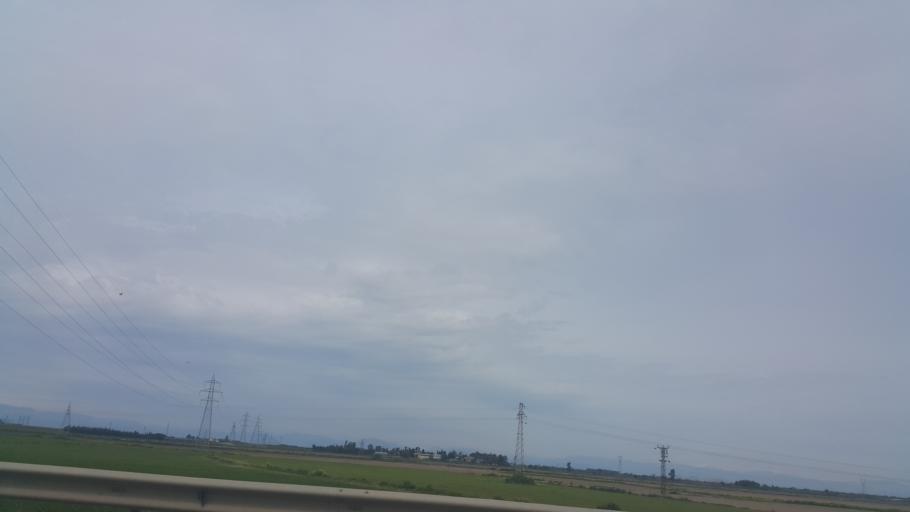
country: TR
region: Adana
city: Ceyhan
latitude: 37.0533
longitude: 35.7940
